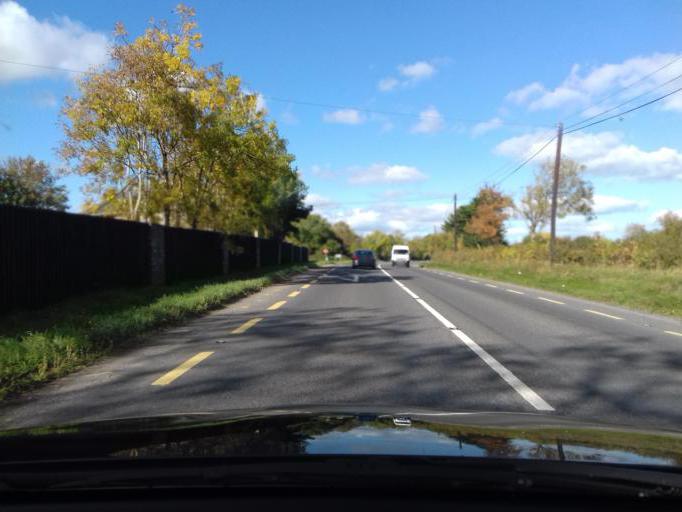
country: IE
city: Kentstown
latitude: 53.6541
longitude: -6.5200
